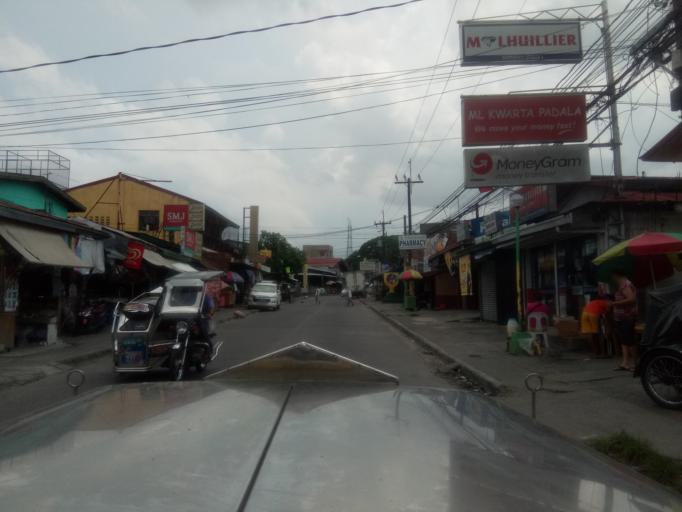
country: PH
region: Calabarzon
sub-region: Province of Cavite
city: Dasmarinas
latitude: 14.3164
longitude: 120.9580
